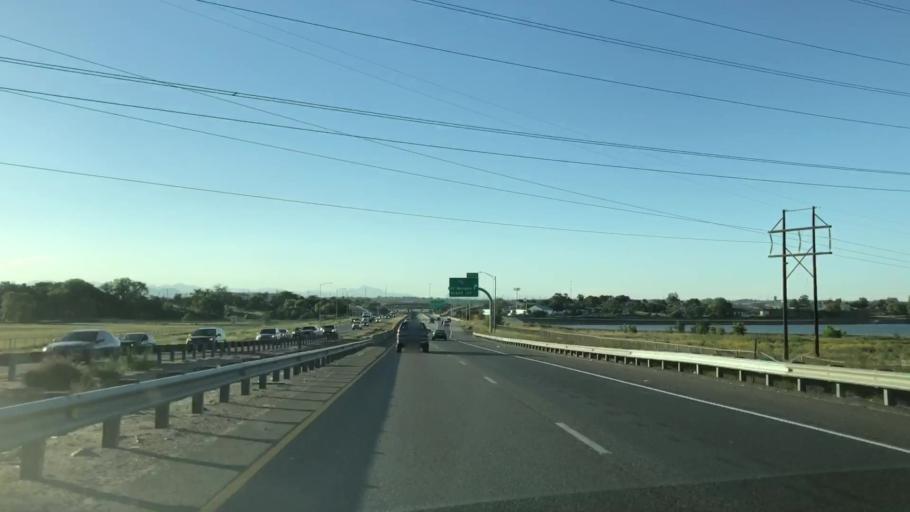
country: US
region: Colorado
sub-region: Adams County
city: Commerce City
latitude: 39.8151
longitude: -104.9519
